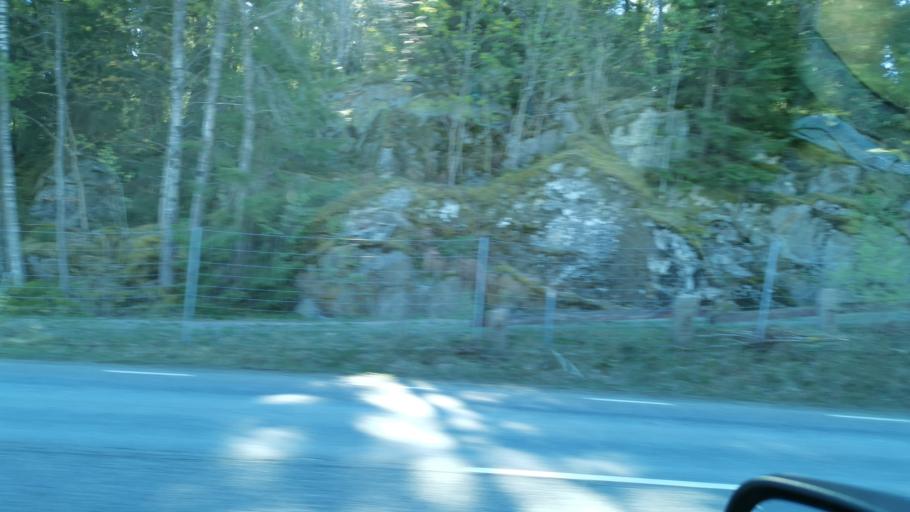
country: SE
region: Vaestra Goetaland
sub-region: Uddevalla Kommun
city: Ljungskile
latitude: 58.2883
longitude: 11.8952
